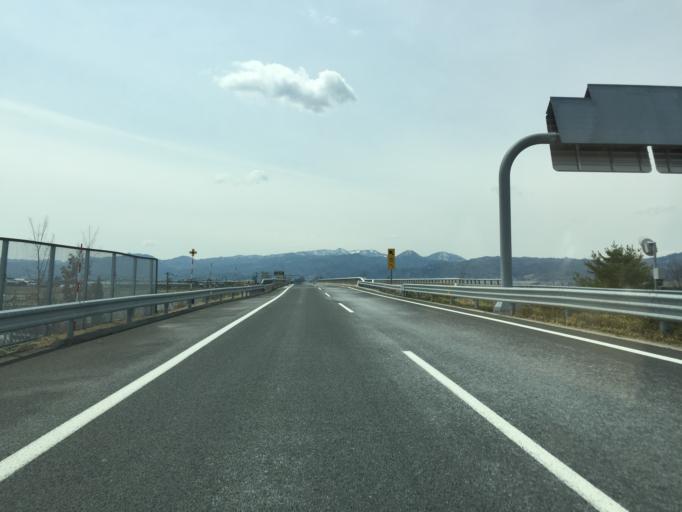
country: JP
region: Yamagata
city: Sagae
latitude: 38.3021
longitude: 140.3088
